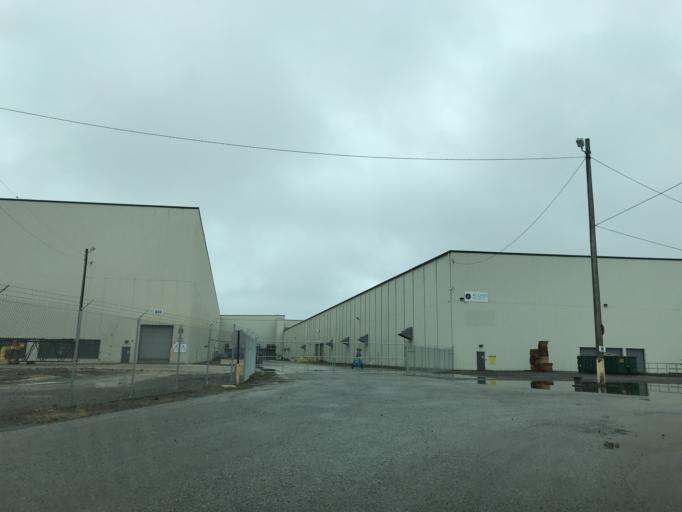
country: US
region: Maryland
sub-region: Baltimore County
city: Edgemere
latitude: 39.2327
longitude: -76.4845
